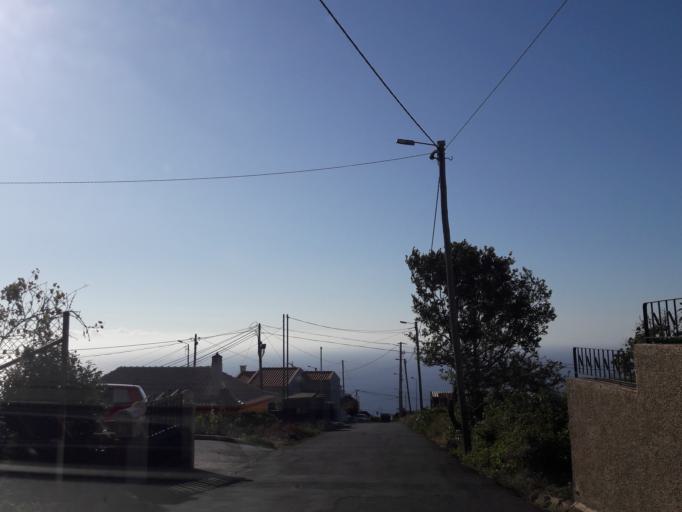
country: PT
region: Madeira
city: Canico
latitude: 32.6520
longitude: -16.8577
